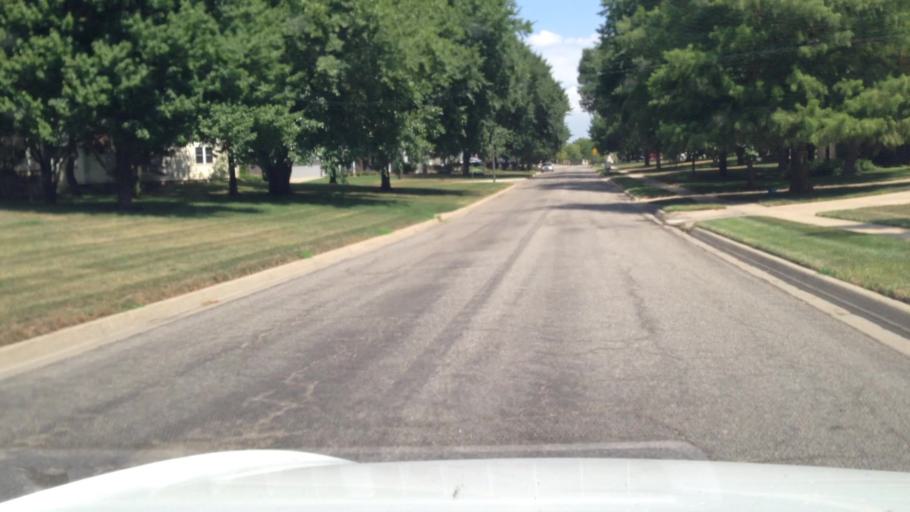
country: US
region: Kansas
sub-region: Douglas County
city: Lawrence
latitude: 38.9494
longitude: -95.3057
